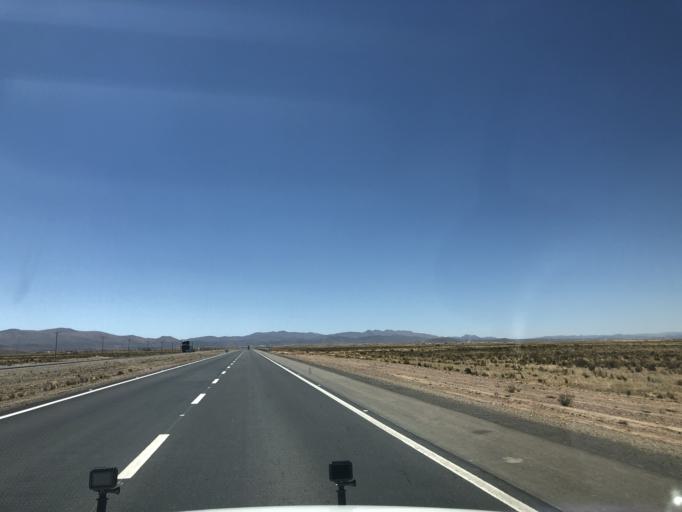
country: BO
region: La Paz
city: Colquiri
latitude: -17.6508
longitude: -67.1809
